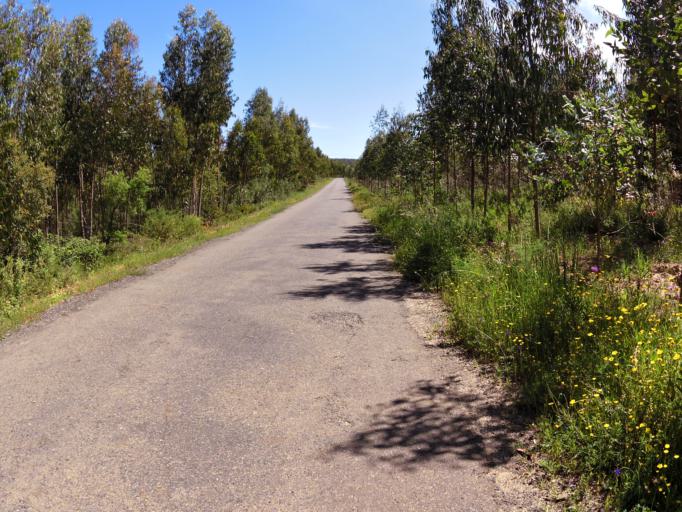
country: PT
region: Setubal
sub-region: Santiago do Cacem
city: Santiago do Cacem
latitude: 37.9461
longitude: -8.7272
